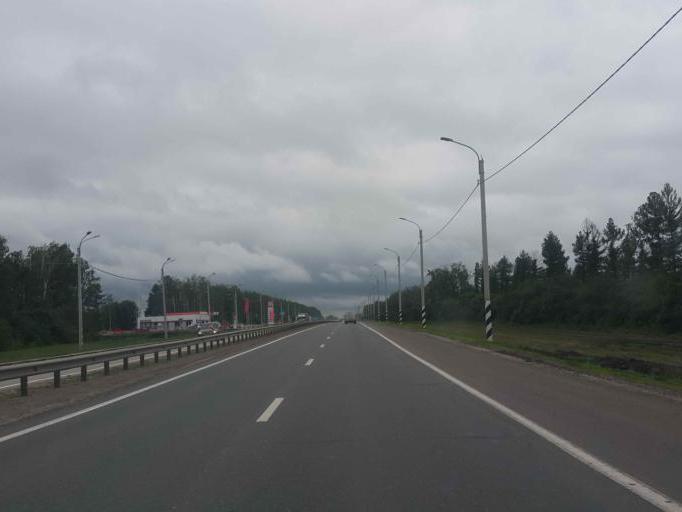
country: RU
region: Tambov
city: Komsomolets
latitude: 52.7352
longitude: 41.2776
